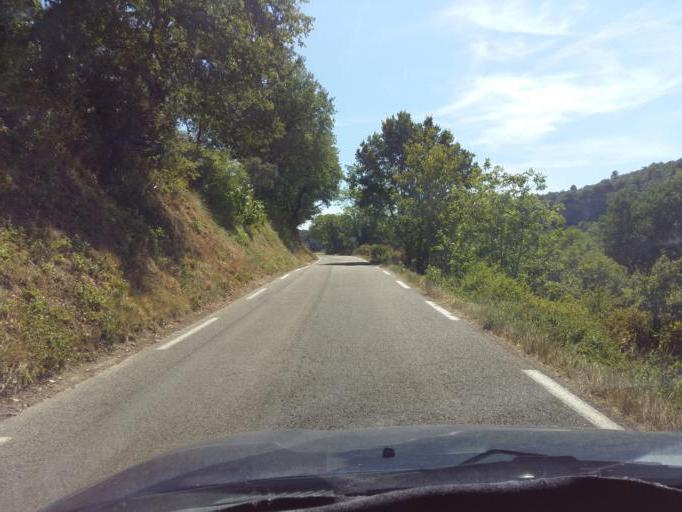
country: FR
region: Provence-Alpes-Cote d'Azur
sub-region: Departement du Vaucluse
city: Venasque
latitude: 43.9992
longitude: 5.1430
